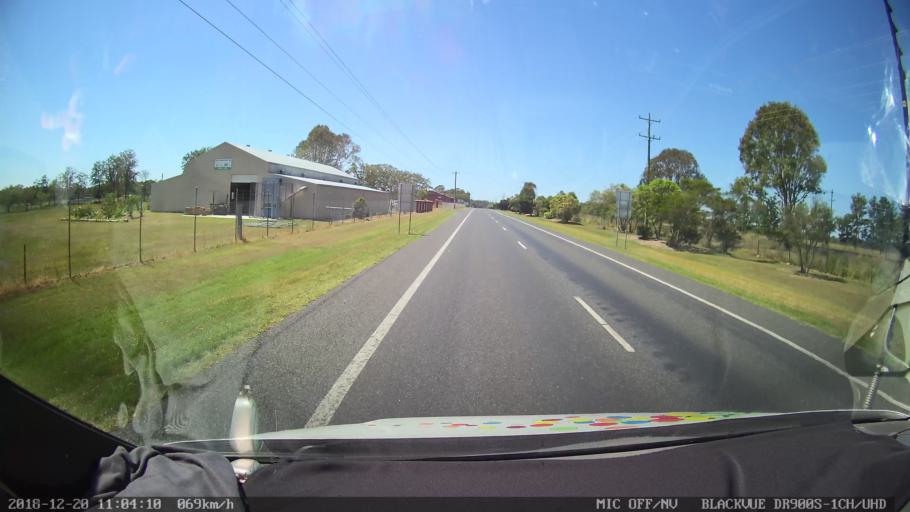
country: AU
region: New South Wales
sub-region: Richmond Valley
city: Casino
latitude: -28.8827
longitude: 153.0441
